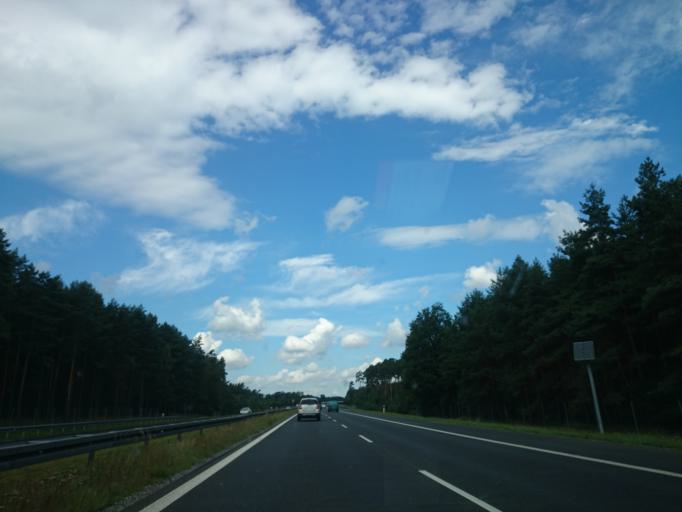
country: PL
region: Opole Voivodeship
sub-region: Powiat opolski
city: Komprachcice
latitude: 50.5870
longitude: 17.8177
